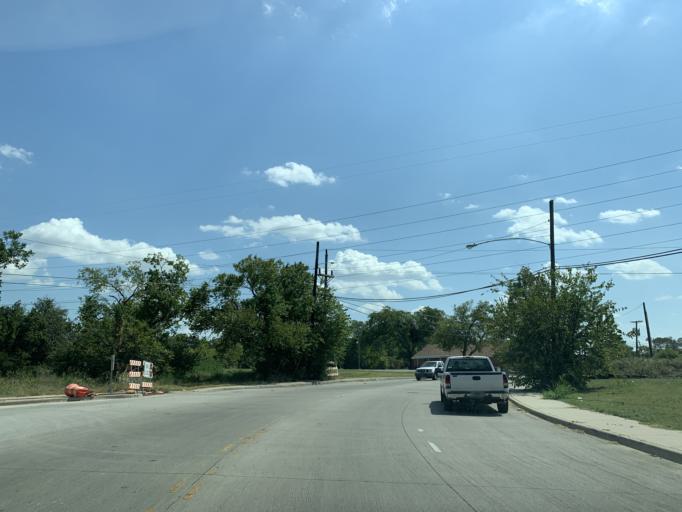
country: US
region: Texas
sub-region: Dallas County
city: Dallas
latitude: 32.7109
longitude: -96.7742
